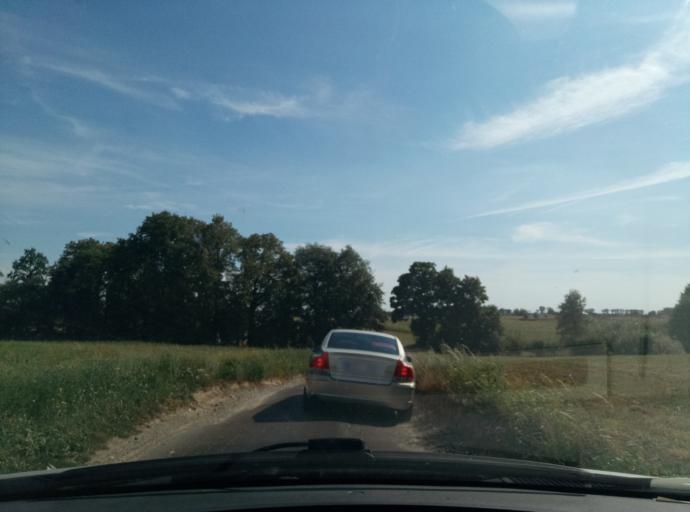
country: PL
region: Kujawsko-Pomorskie
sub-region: Powiat brodnicki
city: Jablonowo Pomorskie
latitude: 53.4103
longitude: 19.2373
